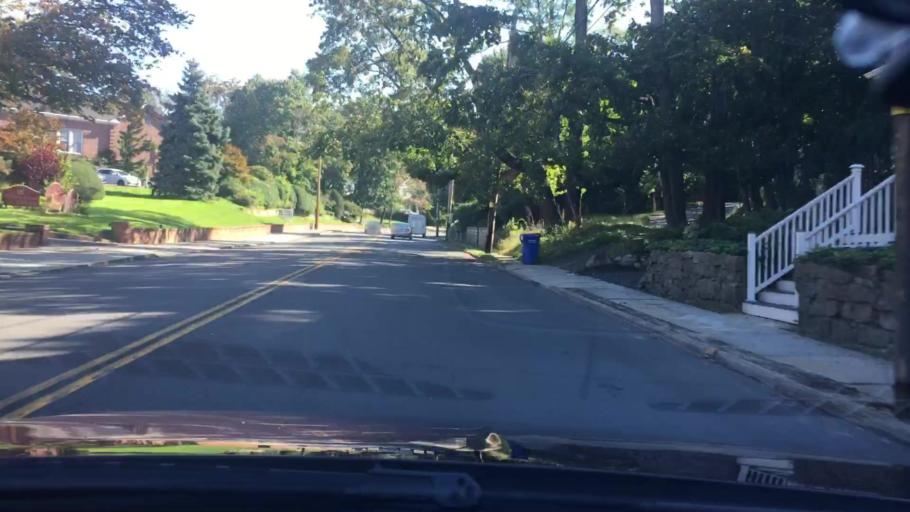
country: US
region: New York
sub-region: Suffolk County
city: Port Jefferson
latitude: 40.9407
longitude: -73.0643
